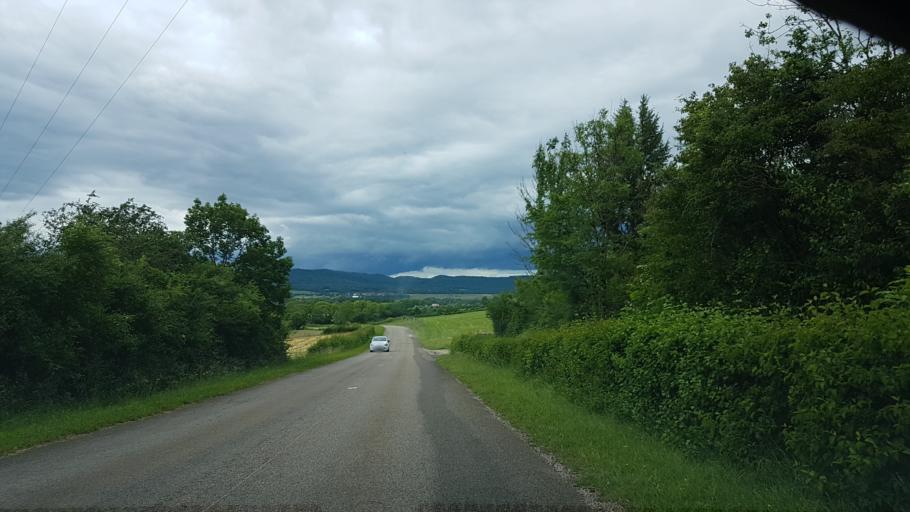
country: FR
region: Franche-Comte
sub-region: Departement du Jura
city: Clairvaux-les-Lacs
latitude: 46.5786
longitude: 5.7346
